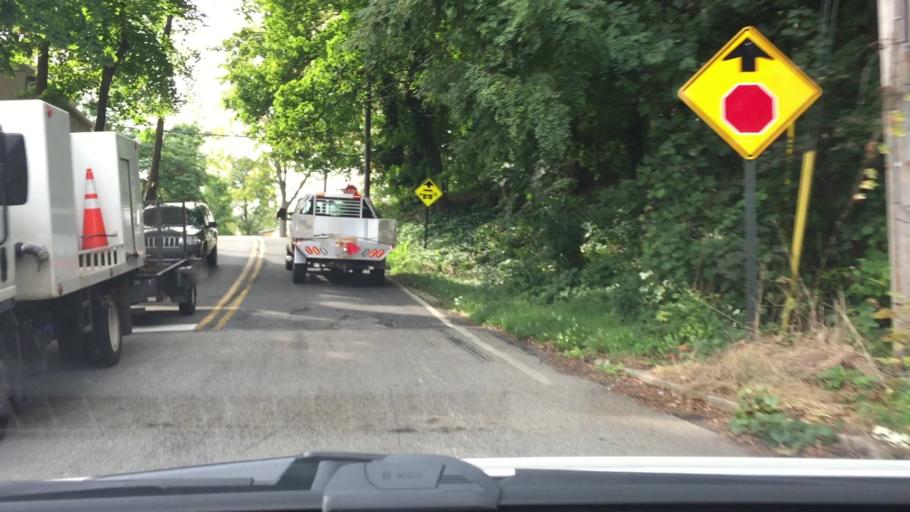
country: US
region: Pennsylvania
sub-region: Delaware County
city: Radnor
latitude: 40.0303
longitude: -75.3665
